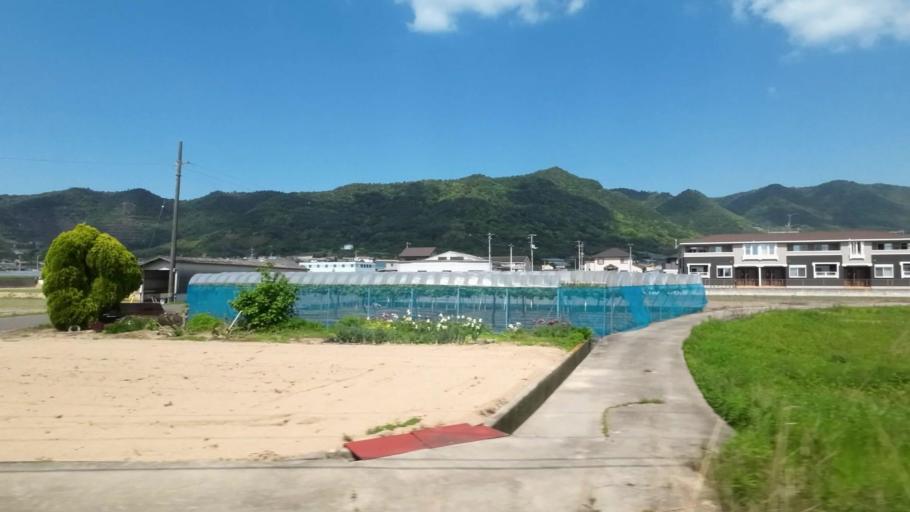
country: JP
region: Kagawa
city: Kan'onjicho
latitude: 34.1543
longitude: 133.6879
